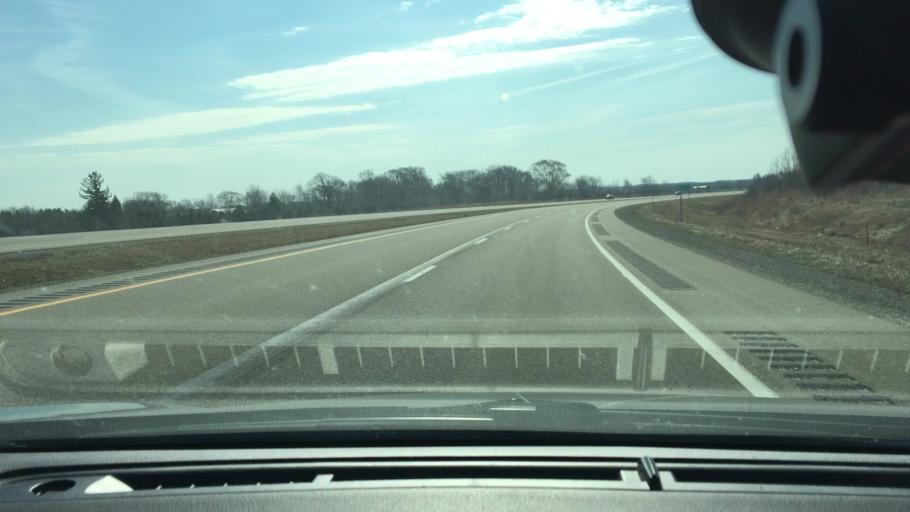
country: US
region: Iowa
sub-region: Floyd County
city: Charles City
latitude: 43.0380
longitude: -92.6569
